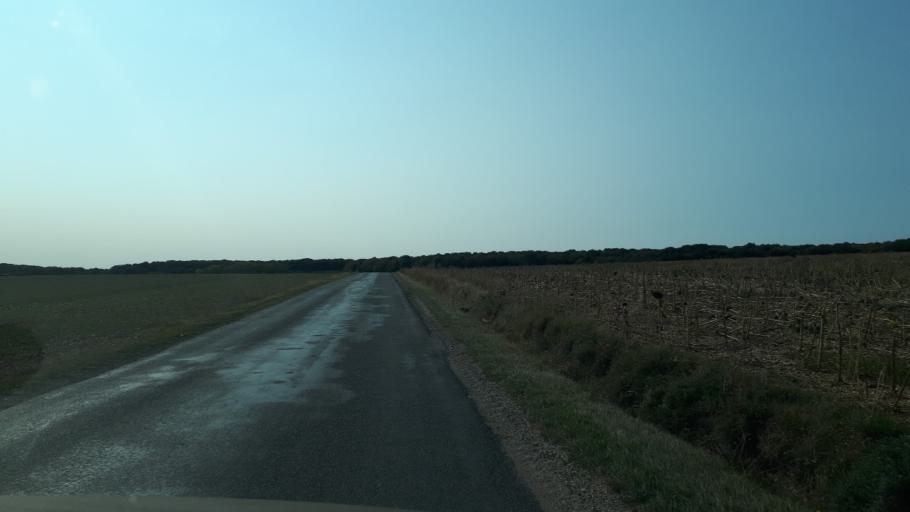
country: FR
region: Centre
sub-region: Departement du Cher
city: Rians
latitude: 47.1853
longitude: 2.6589
